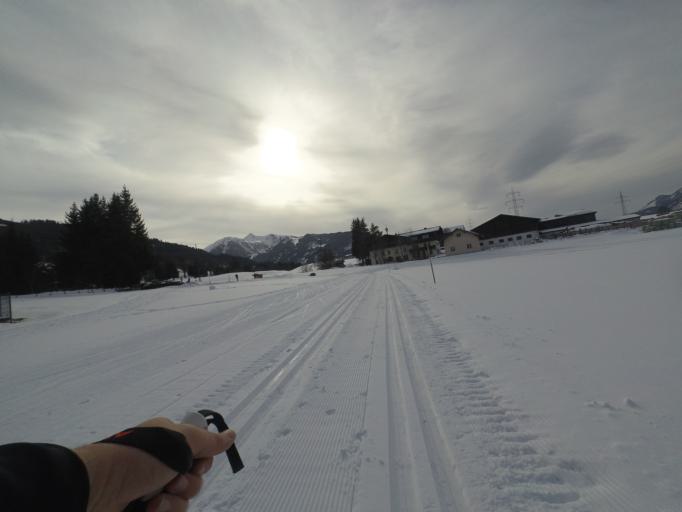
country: AT
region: Salzburg
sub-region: Politischer Bezirk Zell am See
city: Taxenbach
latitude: 47.2901
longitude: 12.9977
